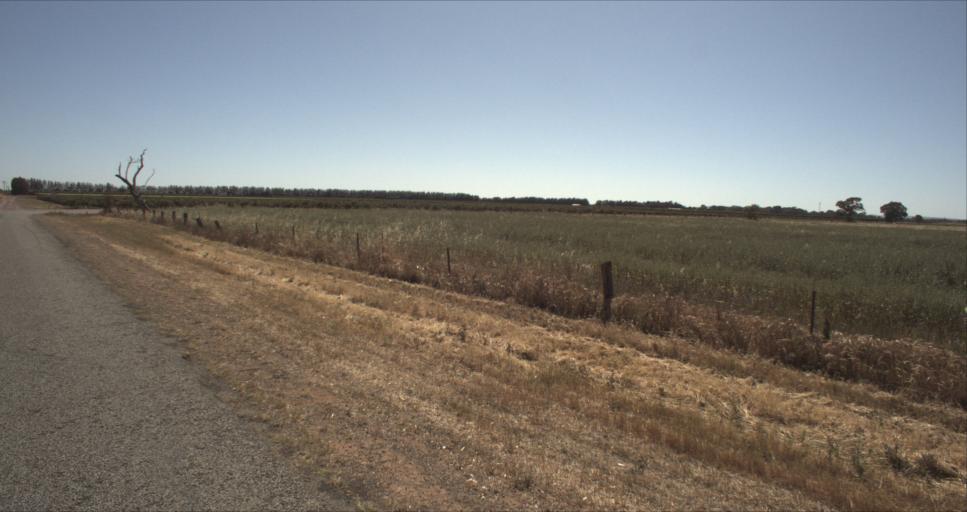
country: AU
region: New South Wales
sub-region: Leeton
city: Leeton
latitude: -34.5338
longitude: 146.3178
